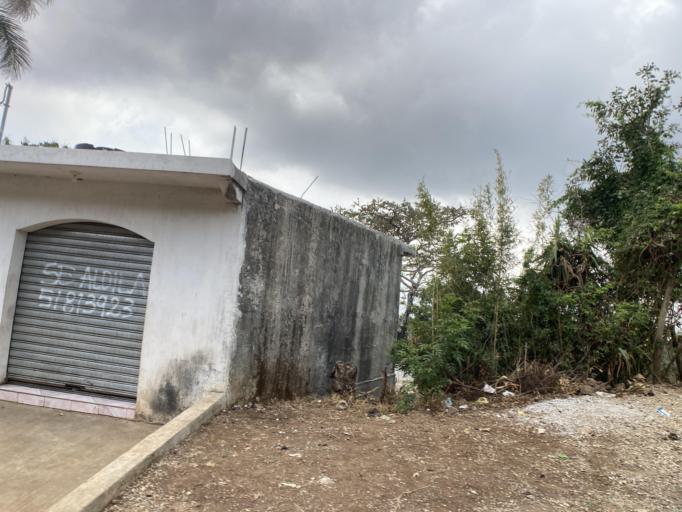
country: GT
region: Escuintla
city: San Vicente Pacaya
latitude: 14.3358
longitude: -90.5672
